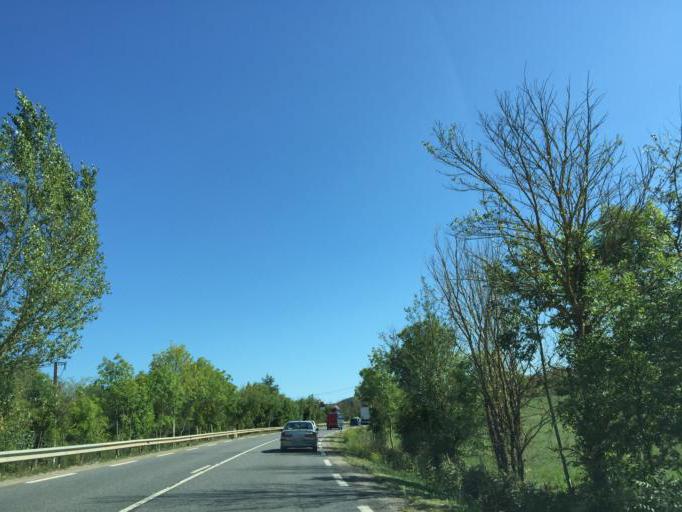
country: FR
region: Midi-Pyrenees
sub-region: Departement de l'Aveyron
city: Severac-le-Chateau
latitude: 44.3397
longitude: 3.0266
